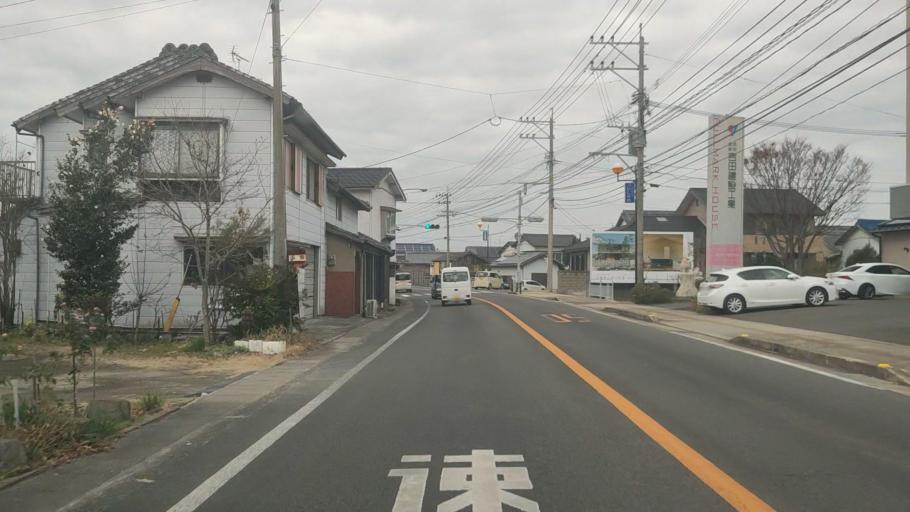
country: JP
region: Nagasaki
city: Shimabara
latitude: 32.8585
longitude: 130.3346
